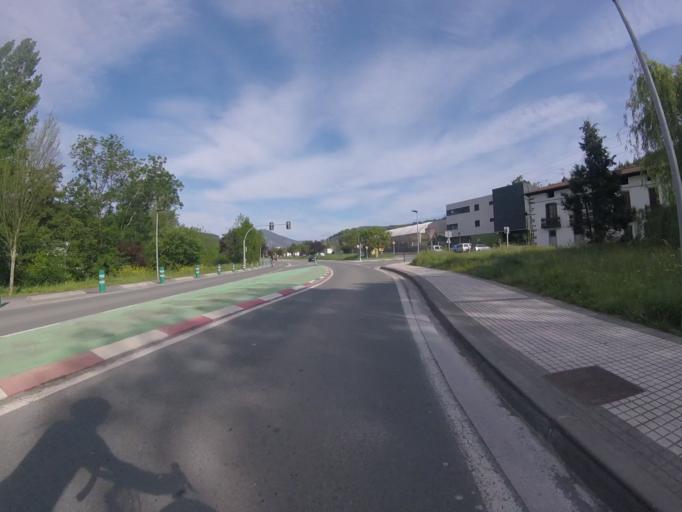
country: ES
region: Basque Country
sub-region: Provincia de Guipuzcoa
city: Gabiria
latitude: 43.0658
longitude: -2.2777
